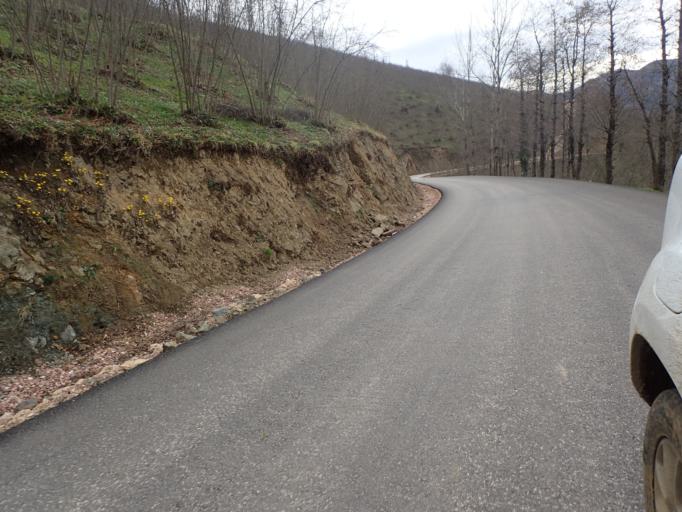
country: TR
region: Ordu
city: Camas
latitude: 40.8897
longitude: 37.5149
